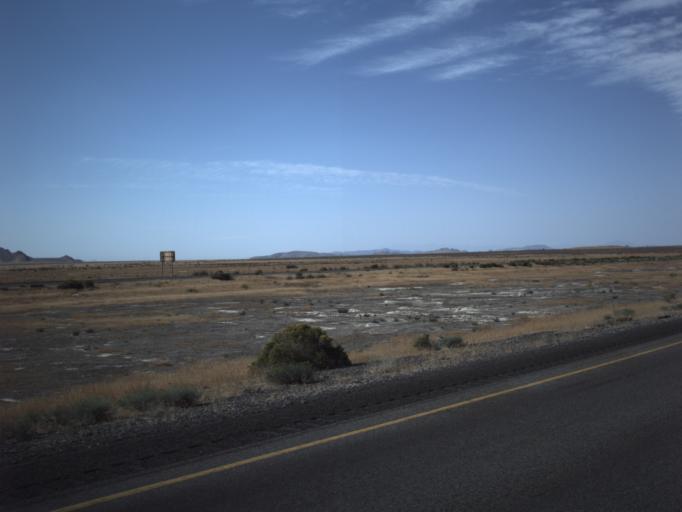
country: US
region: Utah
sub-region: Tooele County
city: Grantsville
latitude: 40.7524
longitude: -113.0412
